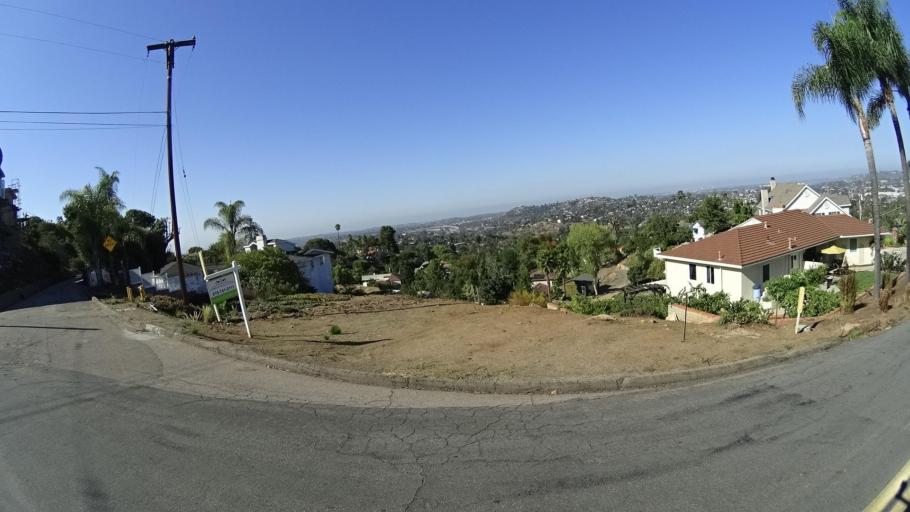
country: US
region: California
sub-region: San Diego County
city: Casa de Oro-Mount Helix
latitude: 32.7690
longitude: -116.9890
